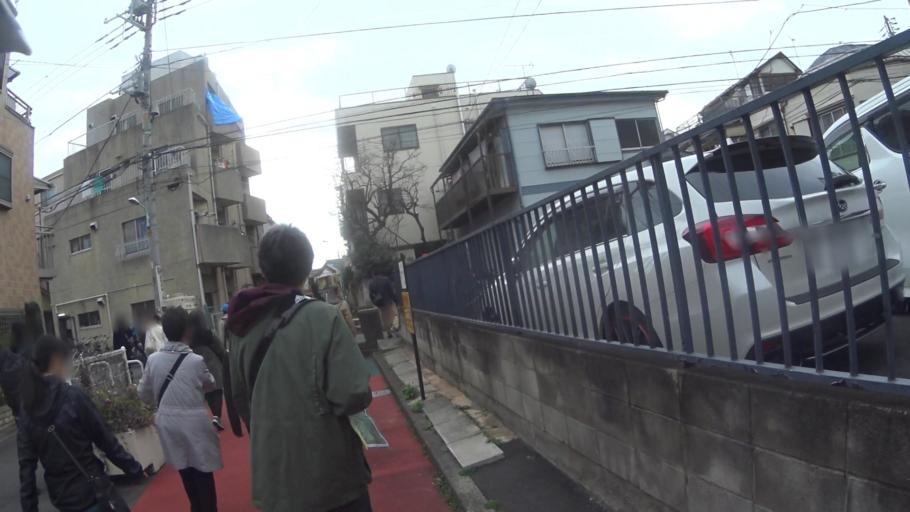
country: JP
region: Tokyo
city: Tokyo
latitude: 35.6871
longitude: 139.6803
